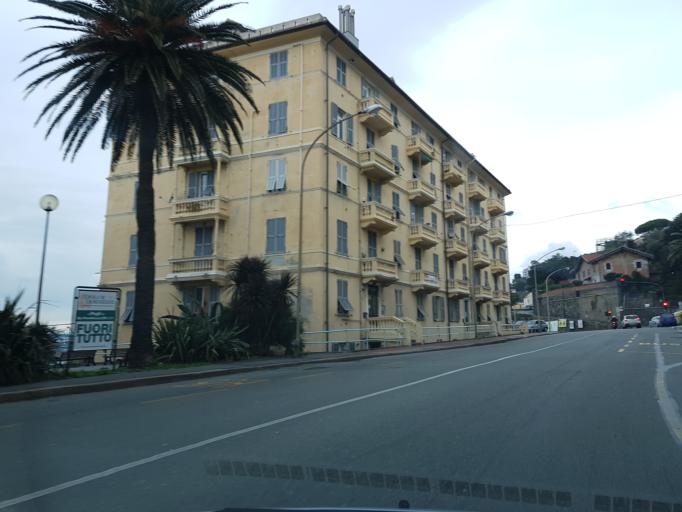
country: IT
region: Liguria
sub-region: Provincia di Genova
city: Mele
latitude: 44.4233
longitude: 8.8075
